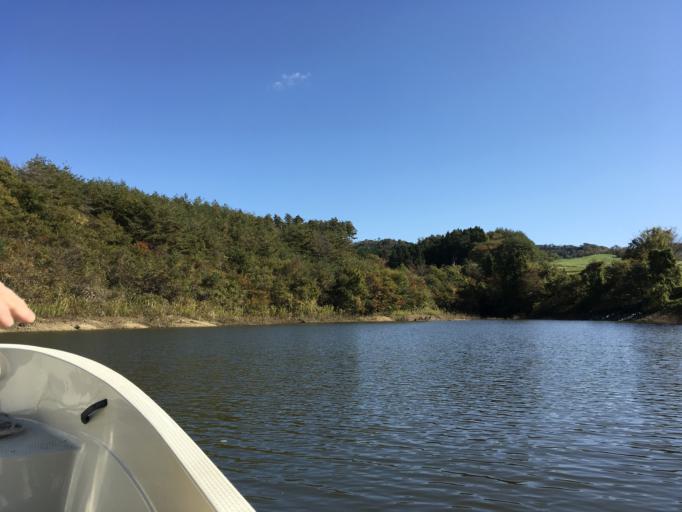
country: JP
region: Iwate
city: Ichinoseki
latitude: 38.7956
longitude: 141.2873
